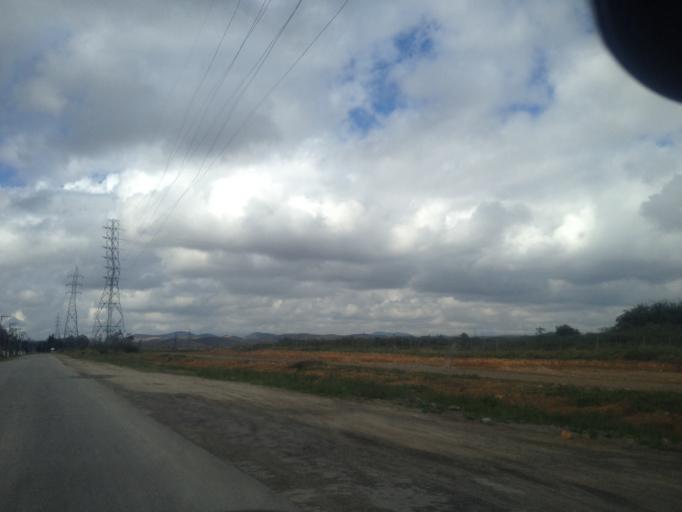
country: BR
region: Rio de Janeiro
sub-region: Porto Real
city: Porto Real
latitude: -22.4412
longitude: -44.3694
